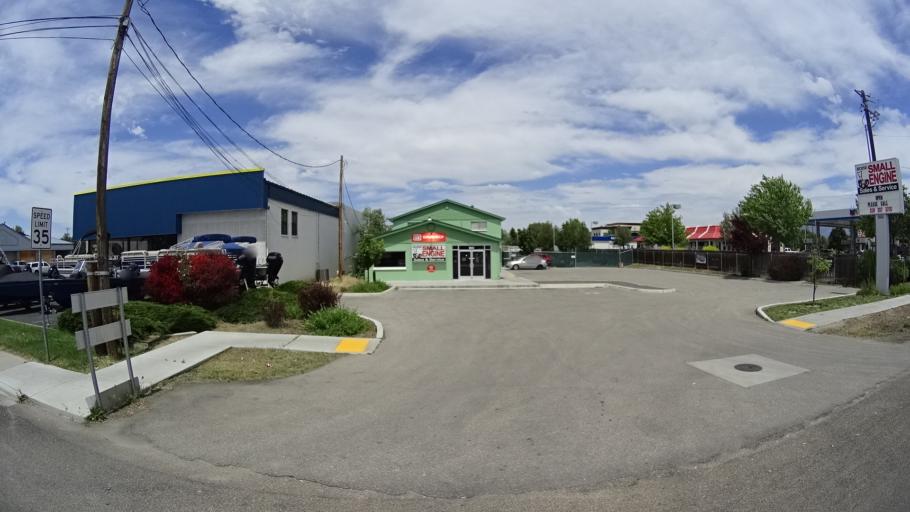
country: US
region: Idaho
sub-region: Ada County
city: Garden City
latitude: 43.6195
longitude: -116.3051
